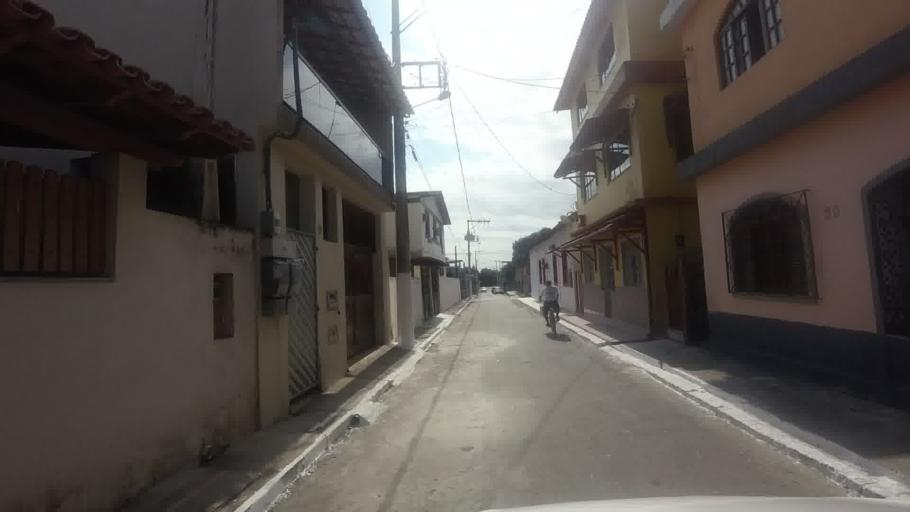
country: BR
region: Espirito Santo
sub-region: Itapemirim
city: Itapemirim
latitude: -21.0078
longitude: -40.8339
